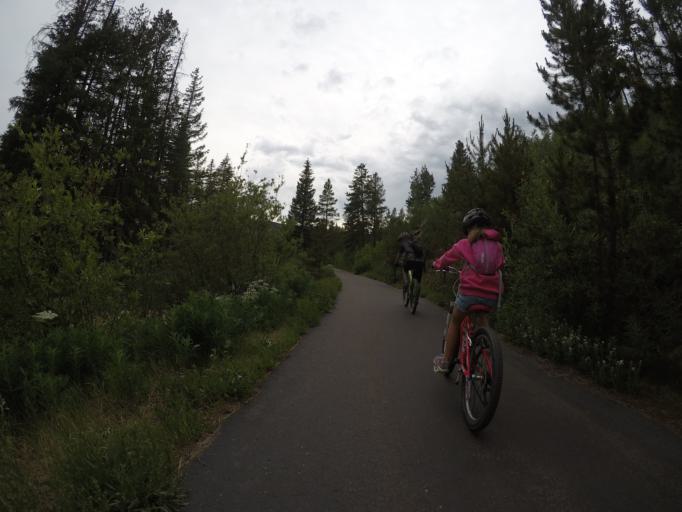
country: US
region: Colorado
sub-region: Grand County
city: Fraser
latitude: 39.8959
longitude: -105.7668
